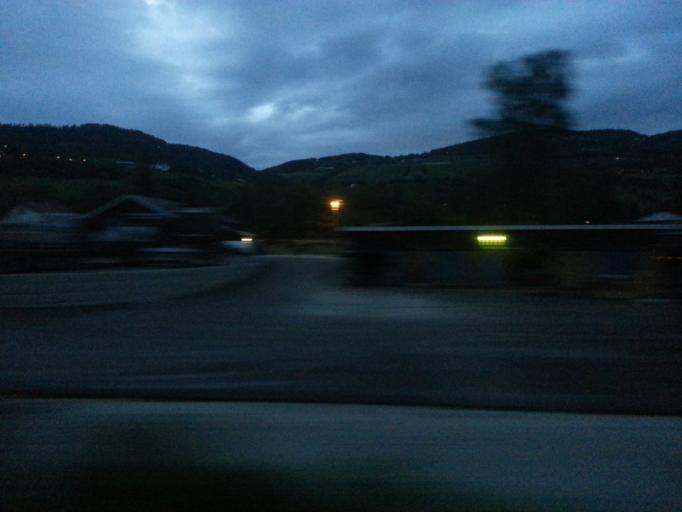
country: NO
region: Oppland
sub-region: Nord-Fron
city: Vinstra
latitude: 61.5869
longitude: 9.7737
